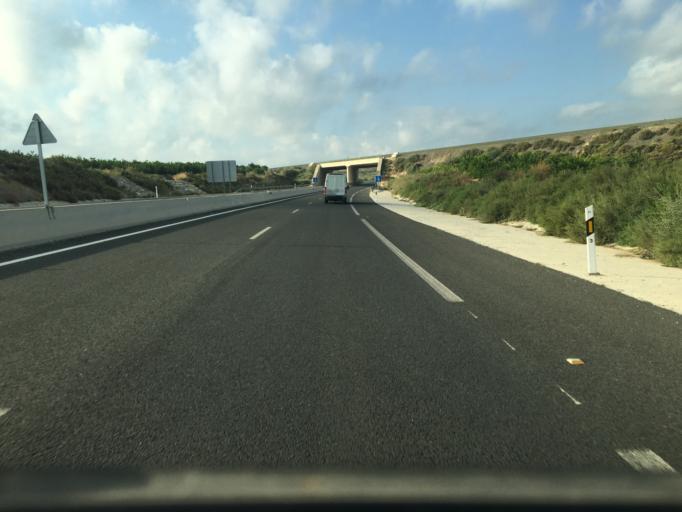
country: ES
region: Murcia
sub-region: Murcia
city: Beniel
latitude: 37.9896
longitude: -0.9746
